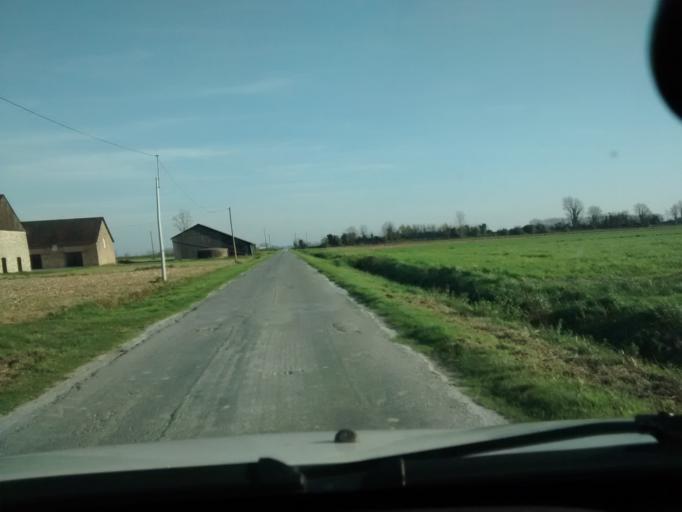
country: FR
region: Brittany
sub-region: Departement d'Ille-et-Vilaine
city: Roz-sur-Couesnon
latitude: 48.6024
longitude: -1.5804
